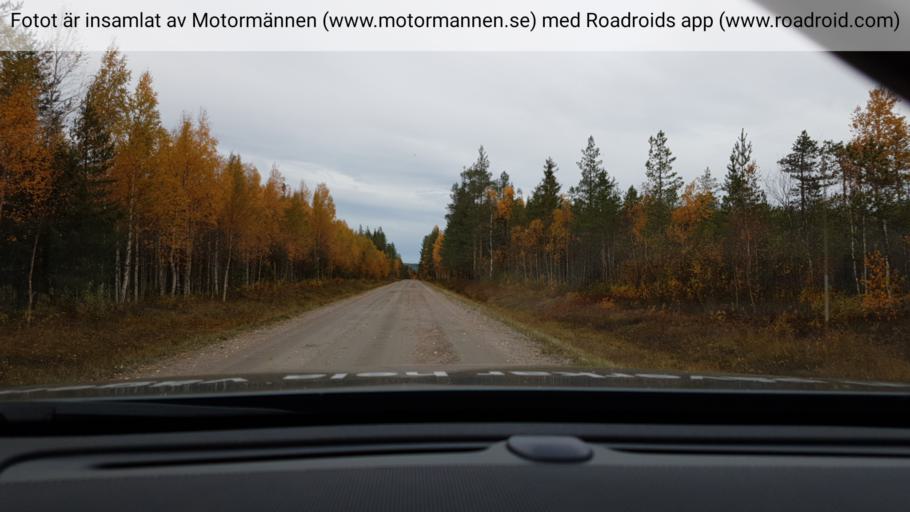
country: SE
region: Norrbotten
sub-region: Overkalix Kommun
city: OEverkalix
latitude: 66.2876
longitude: 22.9681
